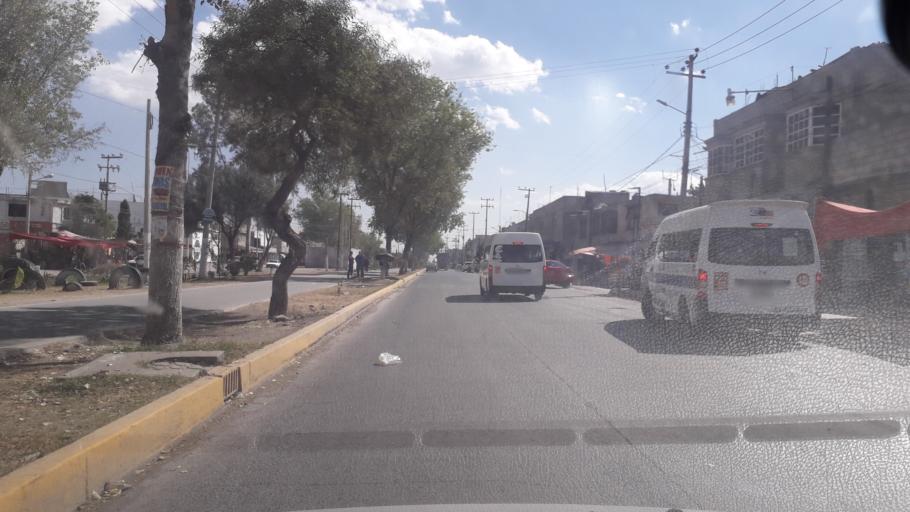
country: MX
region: Mexico
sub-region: Jaltenco
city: Alborada Jaltenco
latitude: 19.6430
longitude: -99.0598
